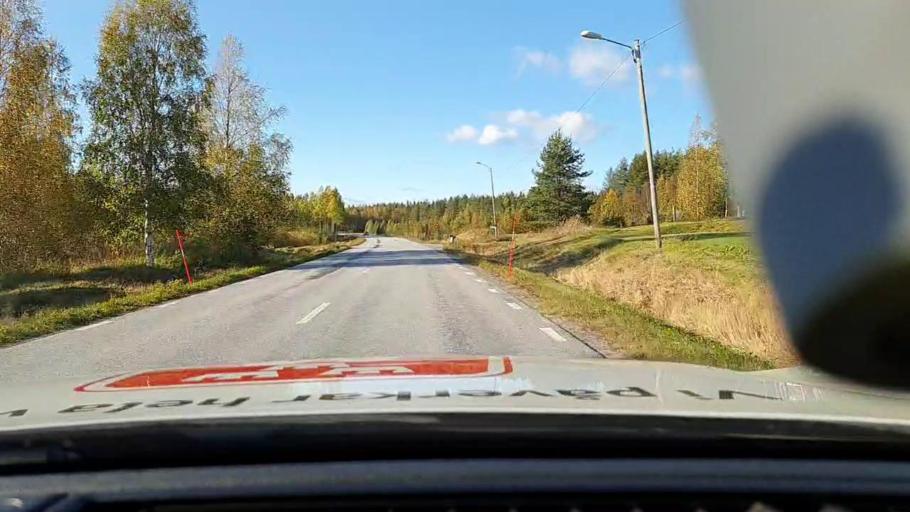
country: SE
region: Norrbotten
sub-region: Pitea Kommun
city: Norrfjarden
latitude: 65.4318
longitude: 21.4884
